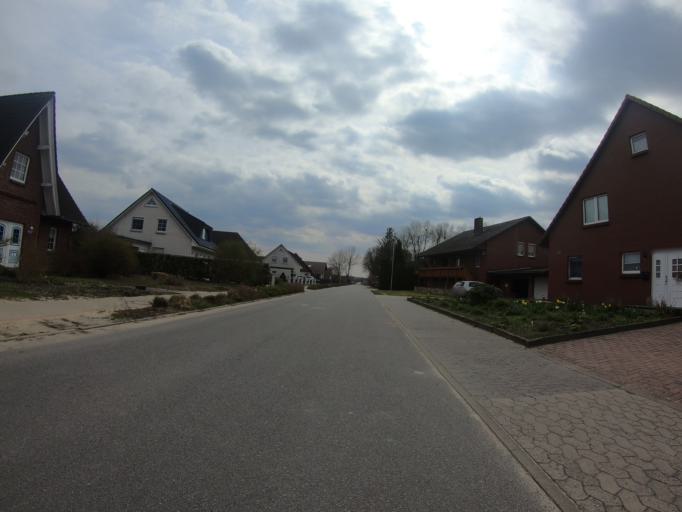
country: DE
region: Lower Saxony
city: Hankensbuttel
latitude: 52.7098
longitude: 10.6207
